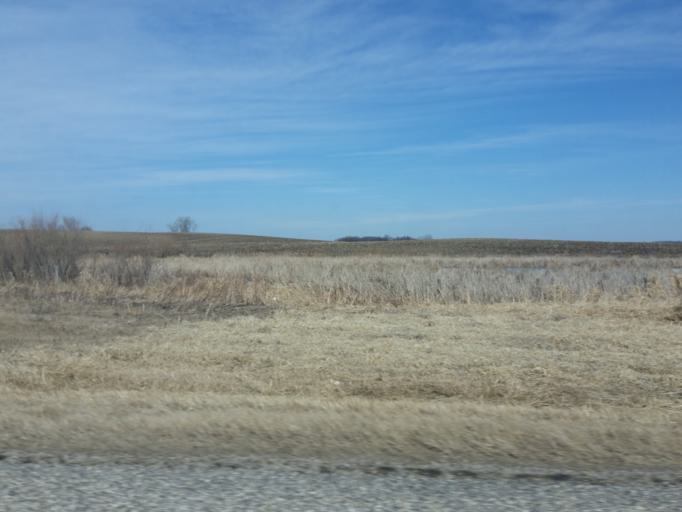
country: US
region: Minnesota
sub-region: Otter Tail County
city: Fergus Falls
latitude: 46.4148
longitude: -96.2135
